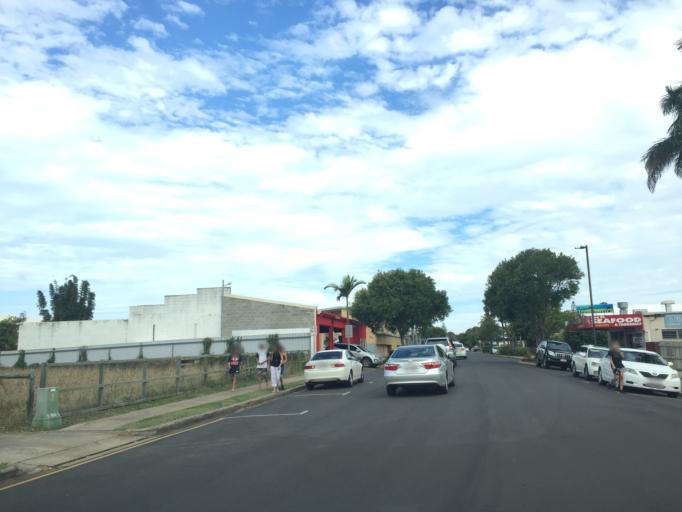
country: AU
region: Queensland
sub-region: Bundaberg
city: Bundaberg
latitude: -24.8139
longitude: 152.4620
